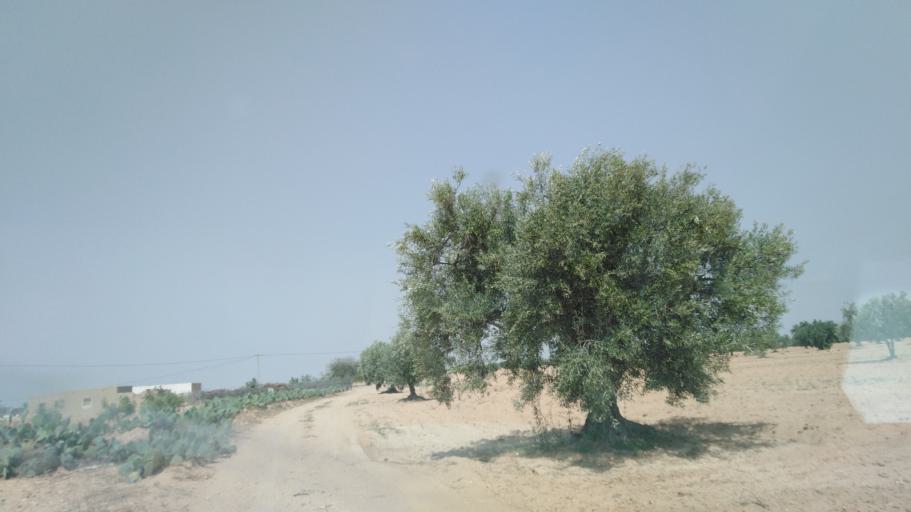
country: TN
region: Safaqis
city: Sfax
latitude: 34.6554
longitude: 10.5550
